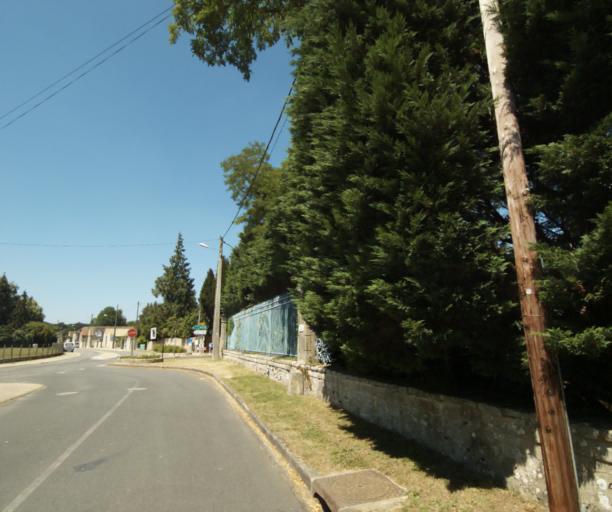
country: FR
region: Ile-de-France
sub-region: Departement de l'Essonne
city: Milly-la-Foret
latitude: 48.3794
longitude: 2.4767
